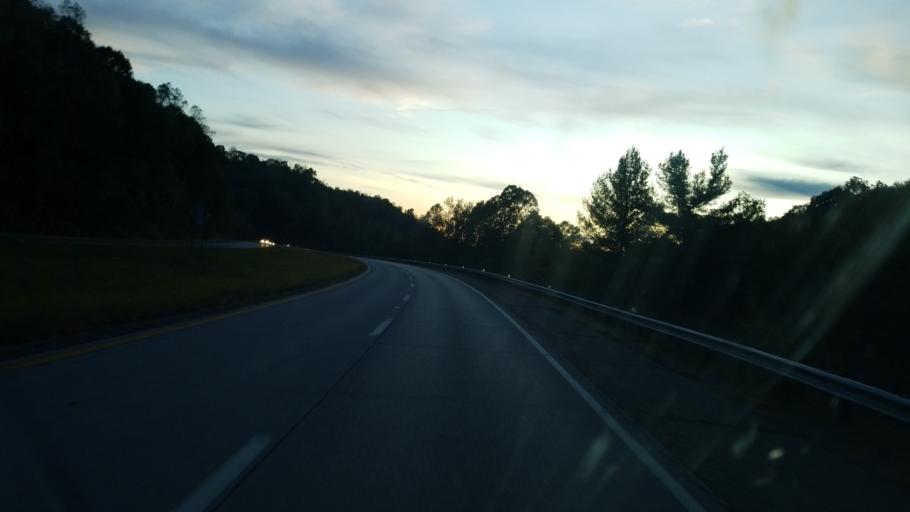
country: US
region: Ohio
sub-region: Meigs County
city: Pomeroy
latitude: 39.0548
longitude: -82.0298
